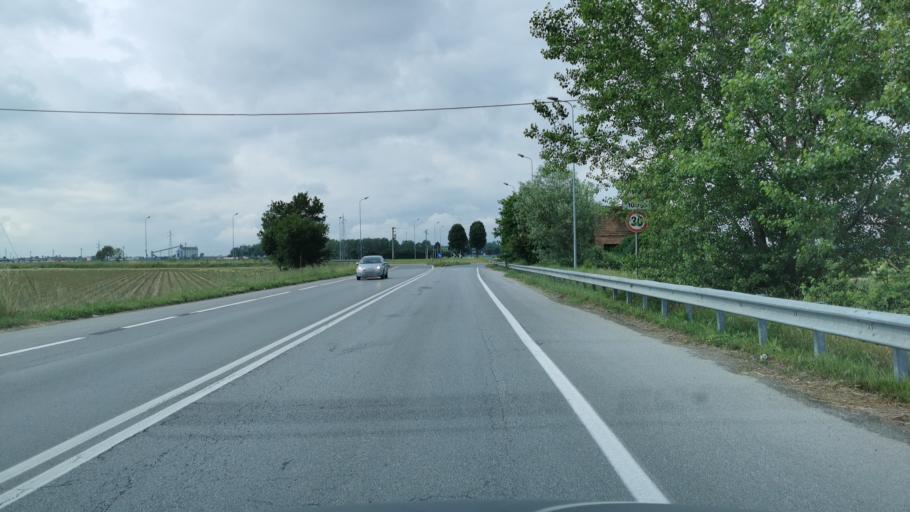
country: IT
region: Piedmont
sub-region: Provincia di Cuneo
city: Racconigi
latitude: 44.8024
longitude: 7.6920
